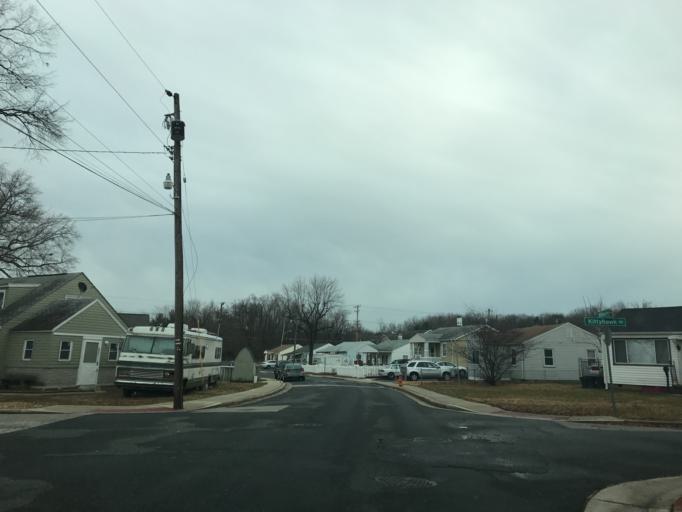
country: US
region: Maryland
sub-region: Baltimore County
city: Middle River
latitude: 39.3241
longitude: -76.4472
